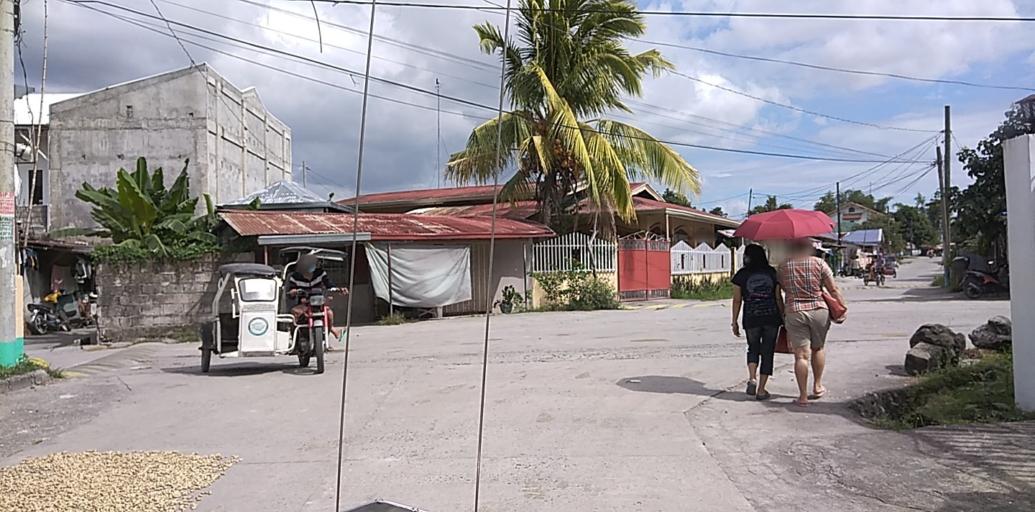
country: PH
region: Central Luzon
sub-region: Province of Pampanga
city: Porac
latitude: 15.0658
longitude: 120.5353
